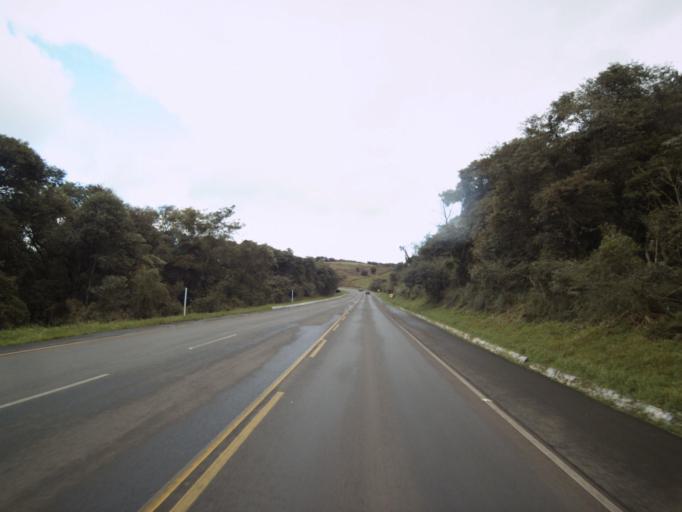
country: BR
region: Santa Catarina
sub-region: Concordia
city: Concordia
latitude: -27.0842
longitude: -51.9080
